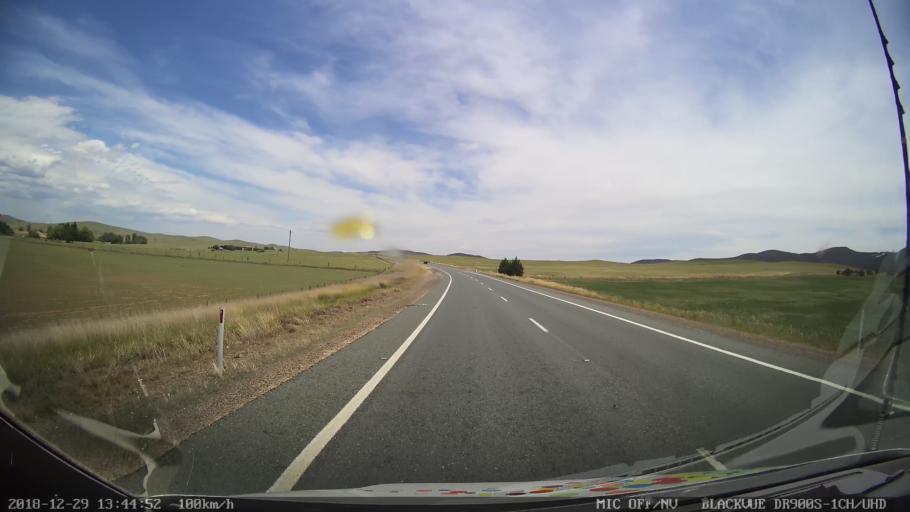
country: AU
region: New South Wales
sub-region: Cooma-Monaro
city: Cooma
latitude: -36.0879
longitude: 149.1465
